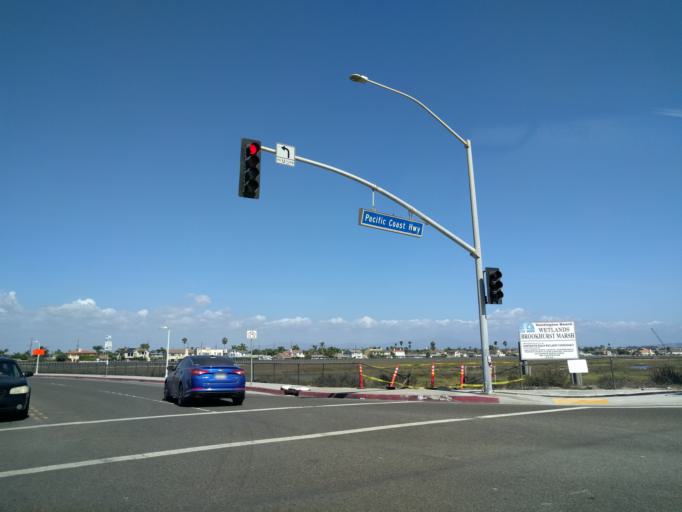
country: US
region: California
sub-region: Orange County
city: Huntington Beach
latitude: 33.6400
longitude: -117.9736
